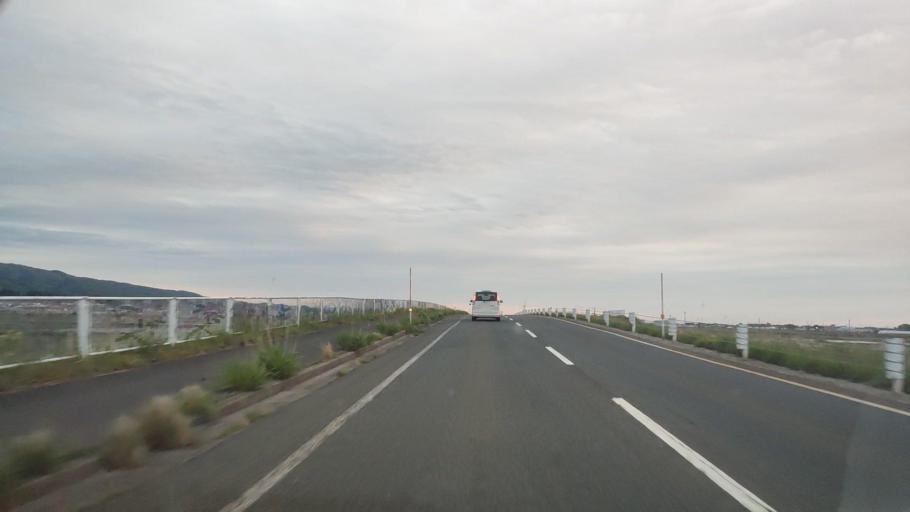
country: JP
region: Niigata
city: Niitsu-honcho
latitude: 37.7594
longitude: 139.0940
